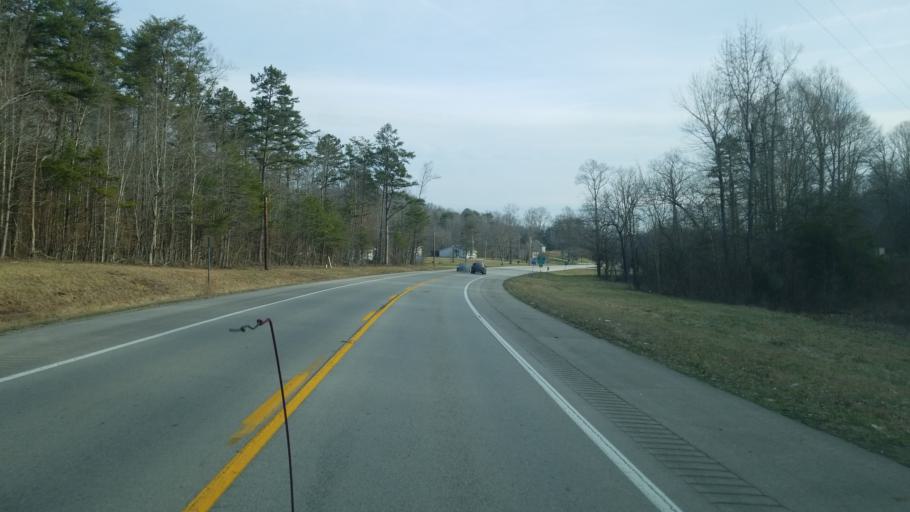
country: US
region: Kentucky
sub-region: Russell County
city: Russell Springs
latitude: 37.1596
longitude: -85.0194
